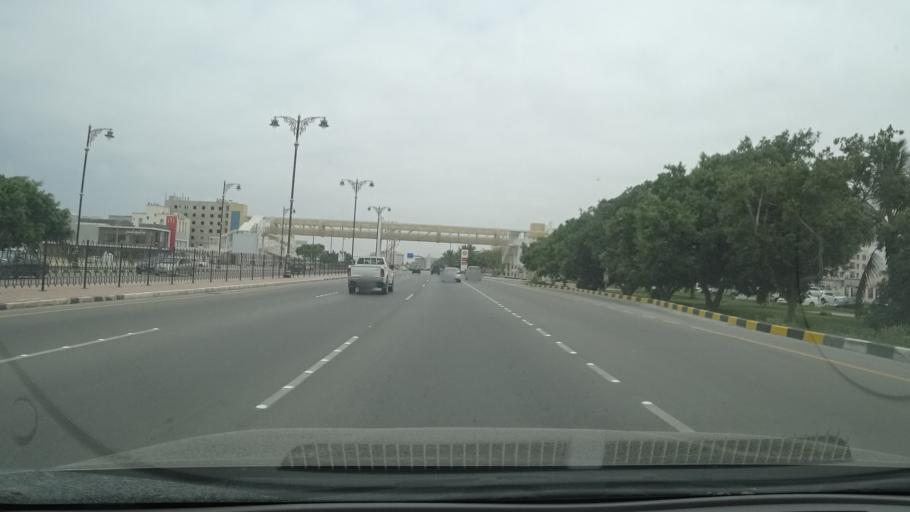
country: OM
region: Zufar
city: Salalah
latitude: 17.0226
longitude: 54.0694
